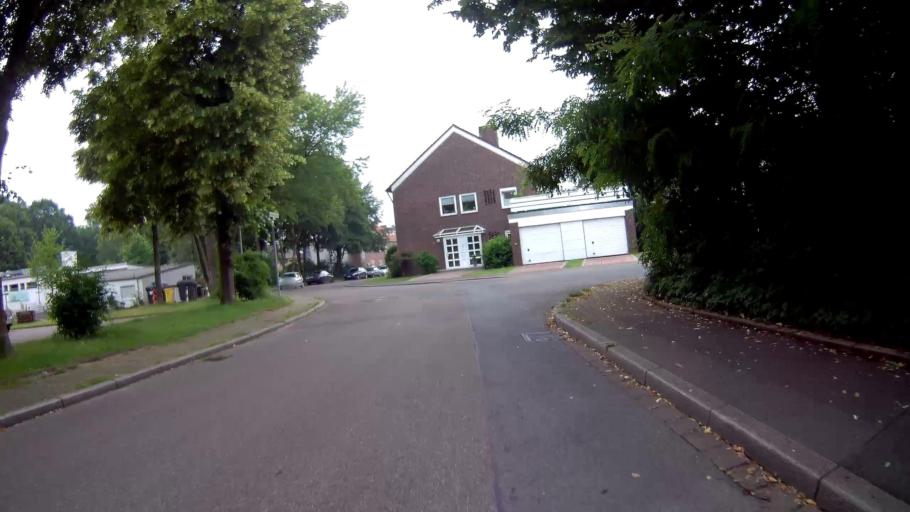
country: DE
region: North Rhine-Westphalia
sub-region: Regierungsbezirk Munster
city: Gladbeck
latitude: 51.5634
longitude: 7.0292
